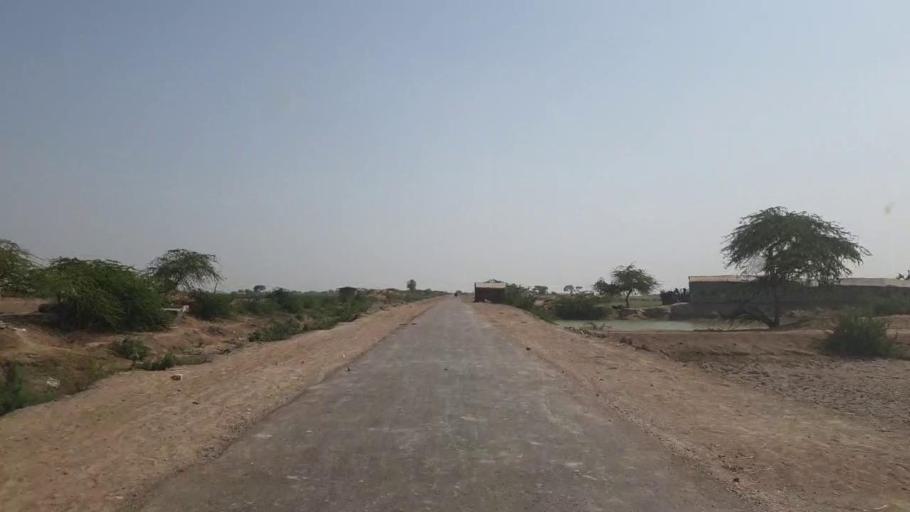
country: PK
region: Sindh
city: Jati
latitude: 24.4595
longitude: 68.5123
